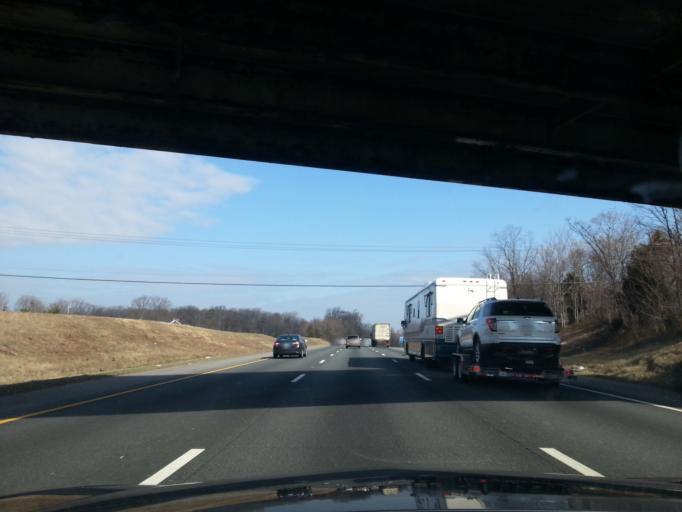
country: US
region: Virginia
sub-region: Stafford County
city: Falmouth
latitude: 38.3134
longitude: -77.5031
